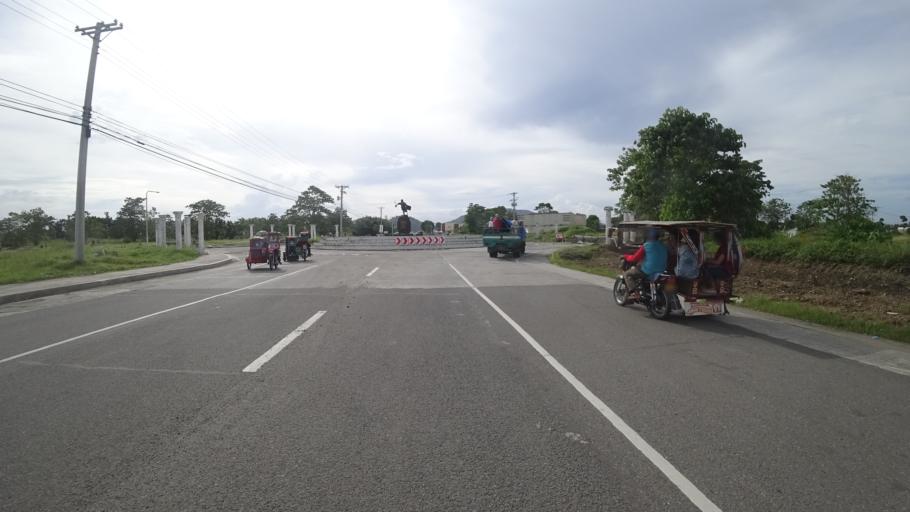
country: PH
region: Eastern Visayas
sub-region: Province of Leyte
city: Pawing
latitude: 11.1762
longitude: 125.0070
